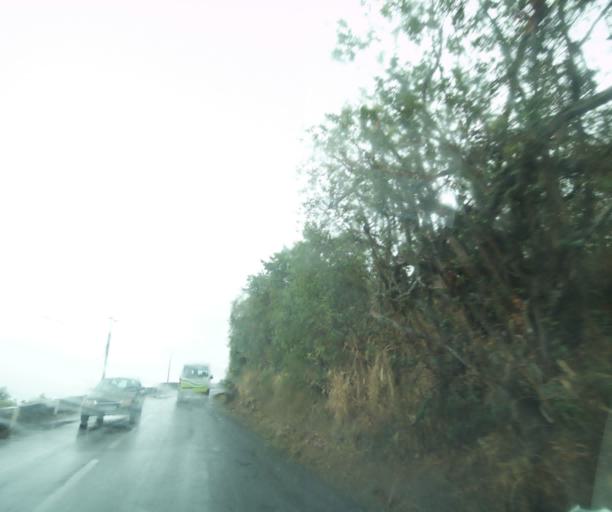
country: RE
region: Reunion
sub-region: Reunion
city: Saint-Paul
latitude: -21.0133
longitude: 55.3109
